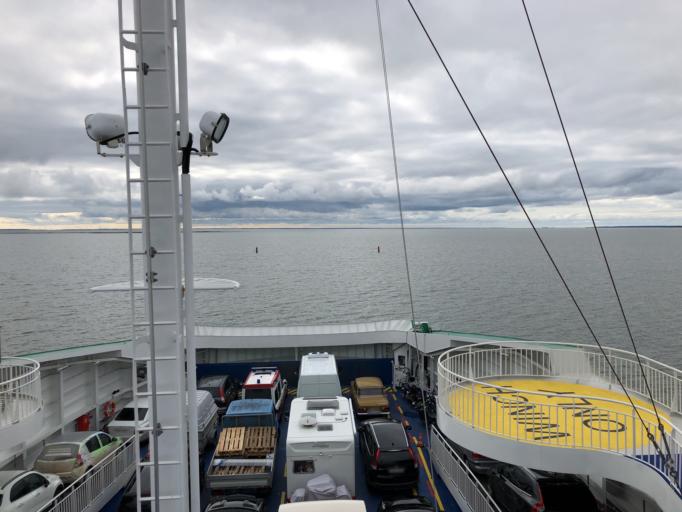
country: EE
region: Laeaene
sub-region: Vormsi vald
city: Hullo
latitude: 58.9079
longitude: 23.3737
